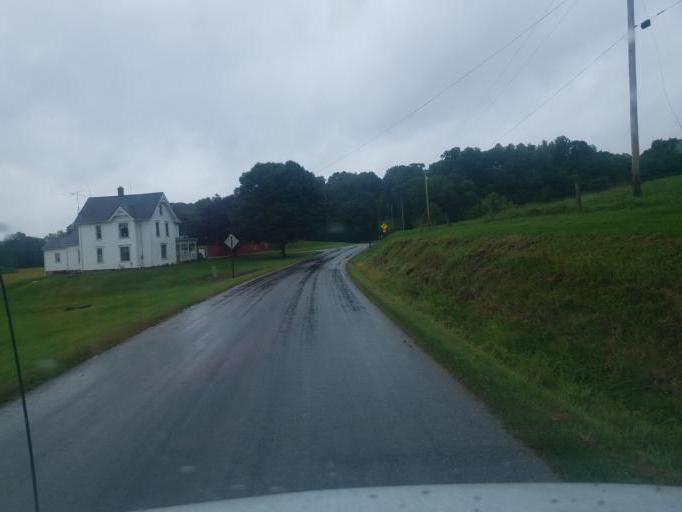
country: US
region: Ohio
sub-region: Wayne County
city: West Salem
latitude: 40.9475
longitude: -82.0296
